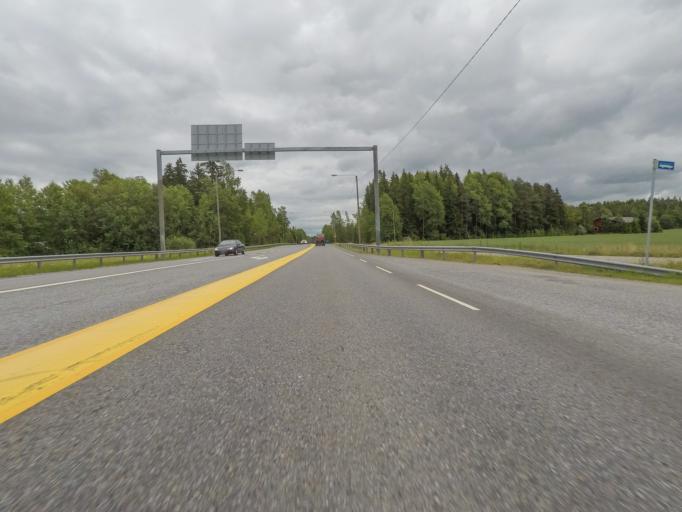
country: FI
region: Varsinais-Suomi
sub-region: Turku
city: Lieto
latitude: 60.4577
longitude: 22.4378
